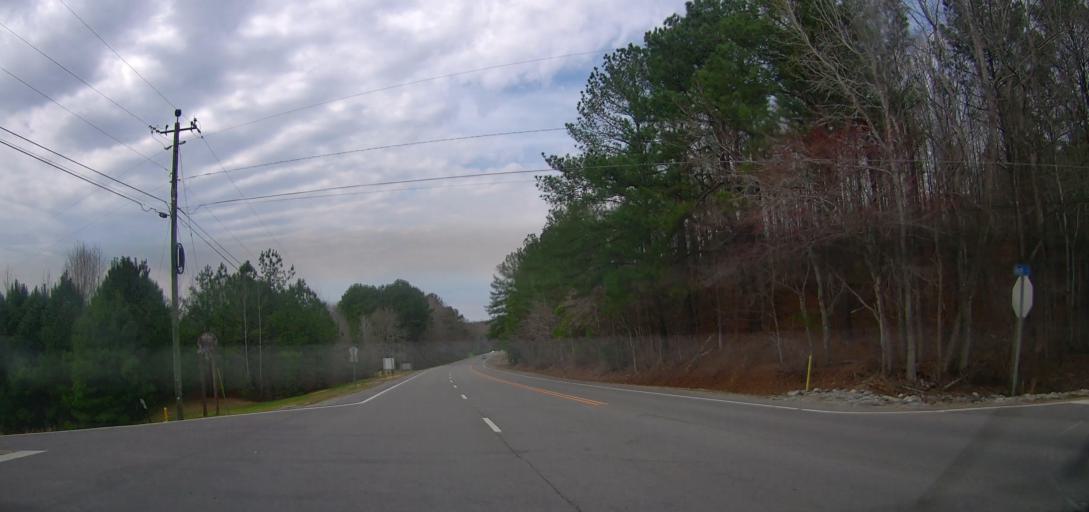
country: US
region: Alabama
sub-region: Marion County
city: Guin
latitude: 33.9896
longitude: -87.9249
